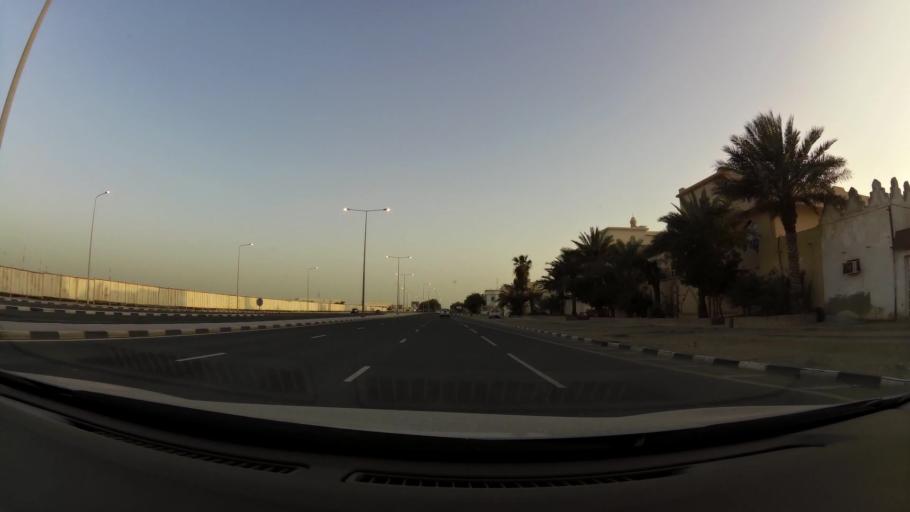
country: QA
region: Baladiyat ad Dawhah
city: Doha
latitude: 25.3206
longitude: 51.4863
